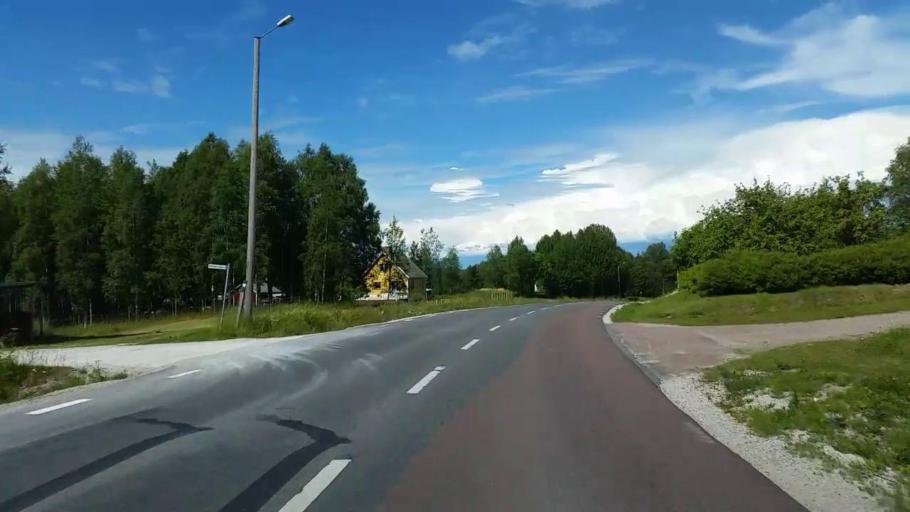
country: SE
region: Dalarna
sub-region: Rattviks Kommun
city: Raettvik
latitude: 61.0408
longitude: 15.1958
